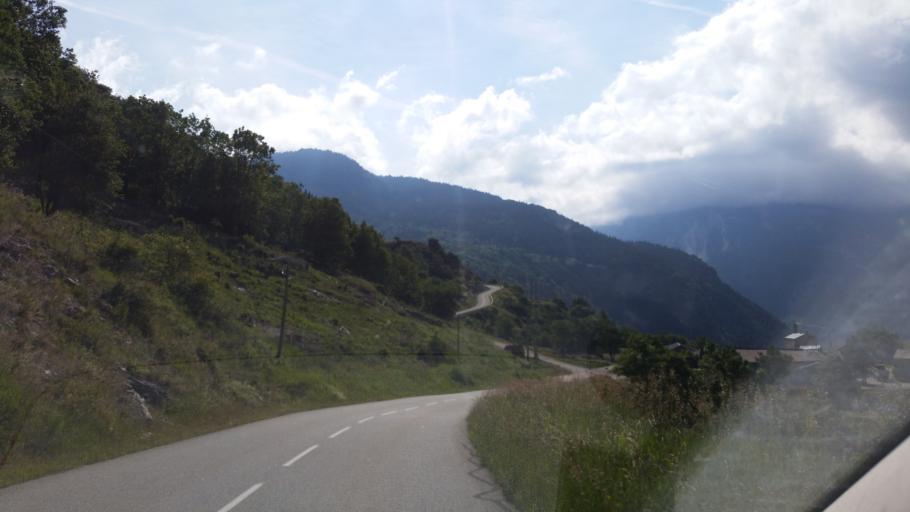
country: FR
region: Rhone-Alpes
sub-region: Departement de la Savoie
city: Modane
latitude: 45.2047
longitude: 6.6128
